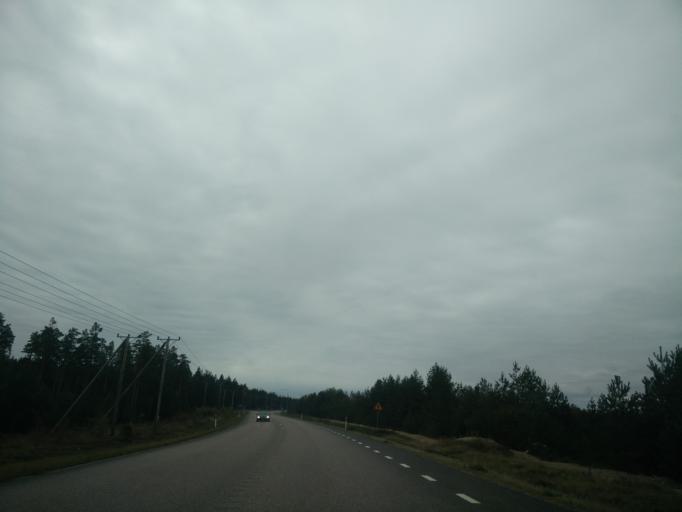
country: SE
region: Gaevleborg
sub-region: Gavle Kommun
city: Gavle
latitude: 60.7976
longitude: 17.2082
